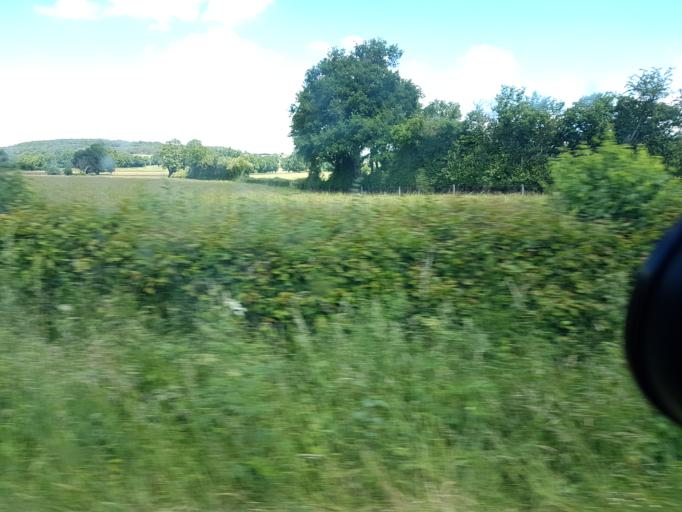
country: FR
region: Bourgogne
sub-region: Departement de Saone-et-Loire
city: Curgy
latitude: 47.0375
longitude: 4.4041
